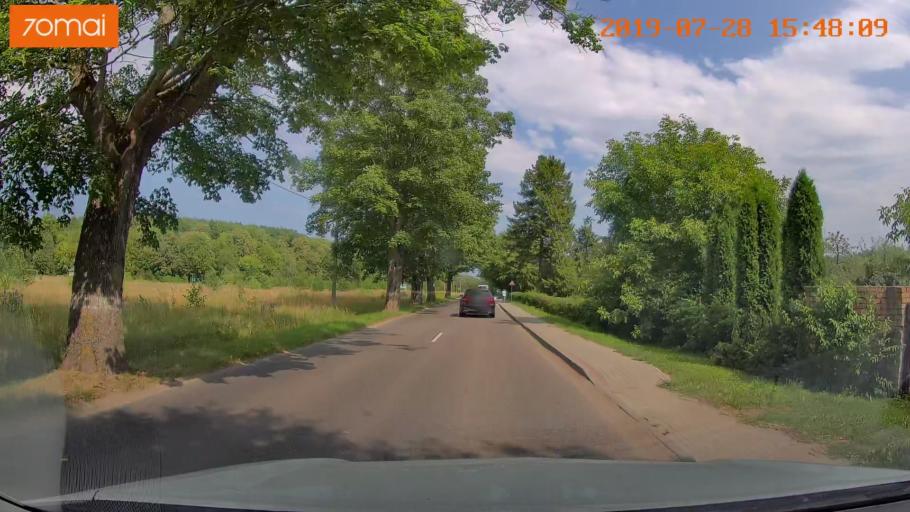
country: RU
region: Kaliningrad
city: Otradnoye
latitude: 54.9434
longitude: 20.0673
